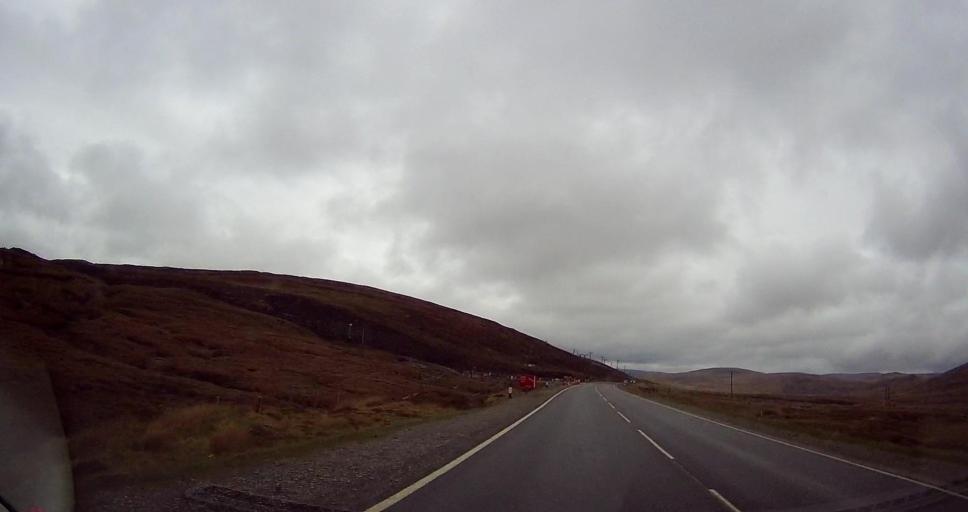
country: GB
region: Scotland
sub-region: Shetland Islands
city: Lerwick
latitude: 60.3282
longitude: -1.2535
